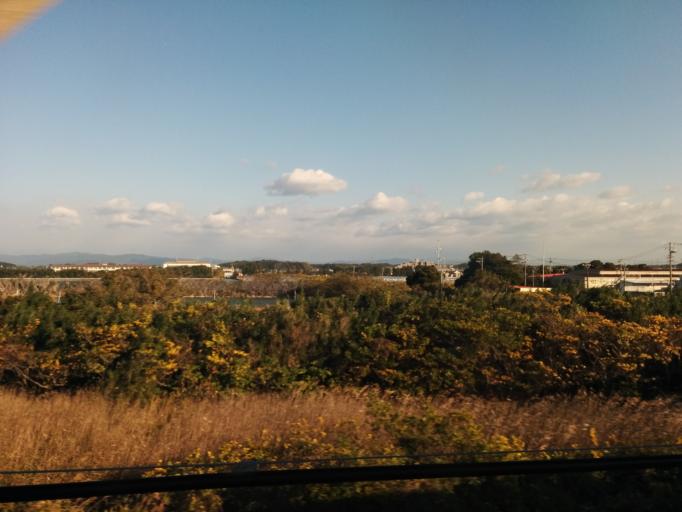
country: JP
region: Shizuoka
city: Hamamatsu
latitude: 34.6872
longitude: 137.6348
